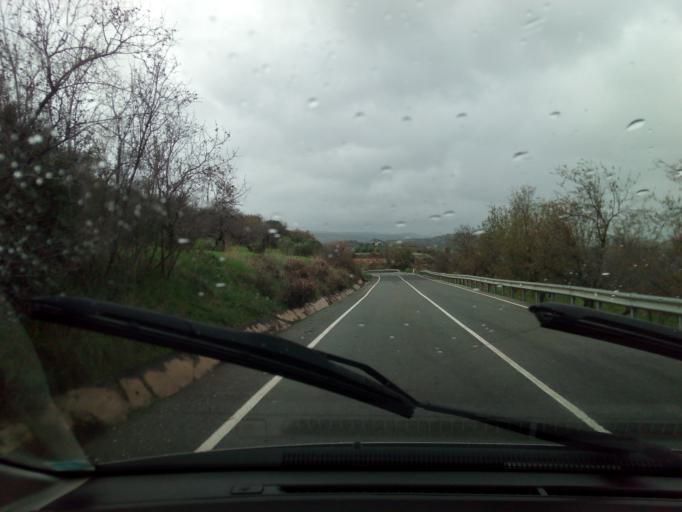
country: CY
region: Pafos
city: Polis
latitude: 34.9507
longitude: 32.4893
